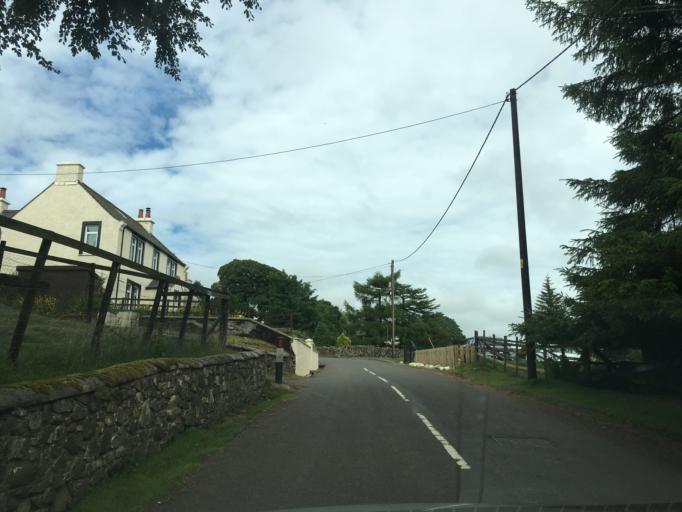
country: GB
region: Scotland
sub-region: Dumfries and Galloway
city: Sanquhar
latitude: 55.3985
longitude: -3.7774
